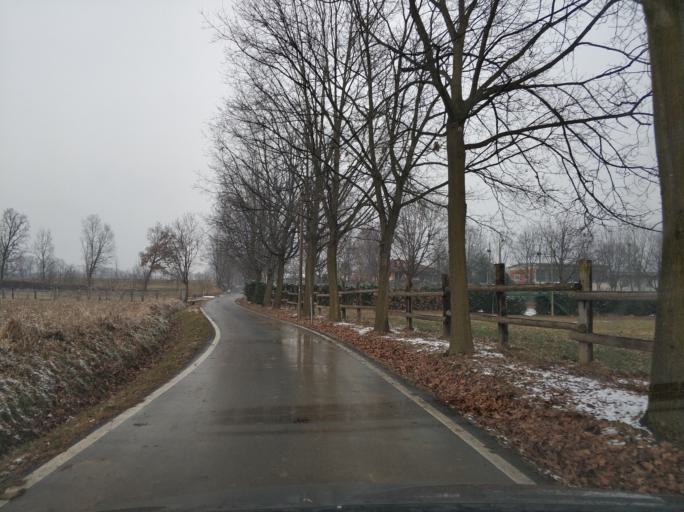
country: IT
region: Piedmont
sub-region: Provincia di Torino
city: San Francesco al Campo
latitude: 45.2222
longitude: 7.6797
